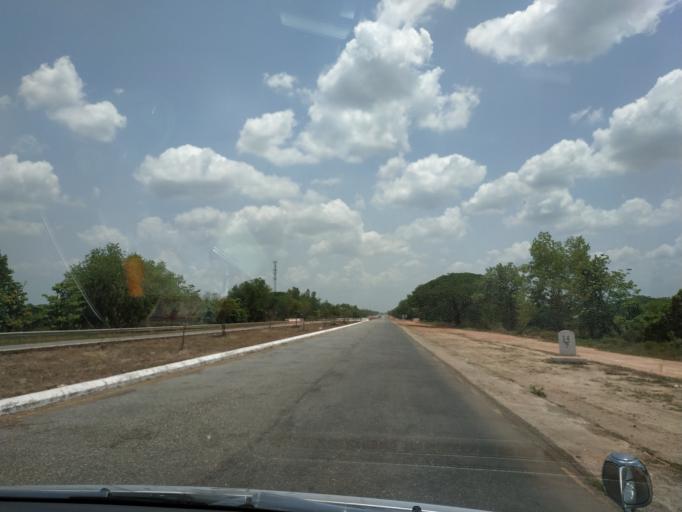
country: MM
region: Bago
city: Thanatpin
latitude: 17.2571
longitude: 96.2300
